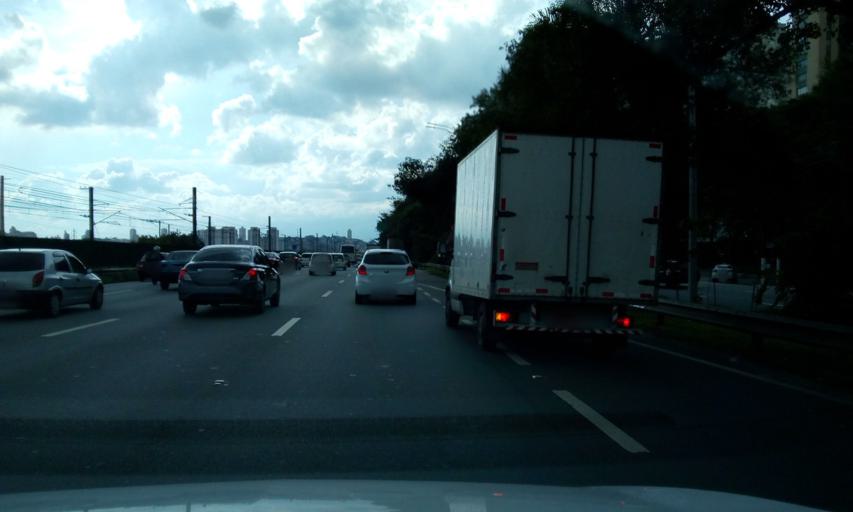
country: BR
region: Sao Paulo
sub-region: Osasco
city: Osasco
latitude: -23.5539
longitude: -46.7188
